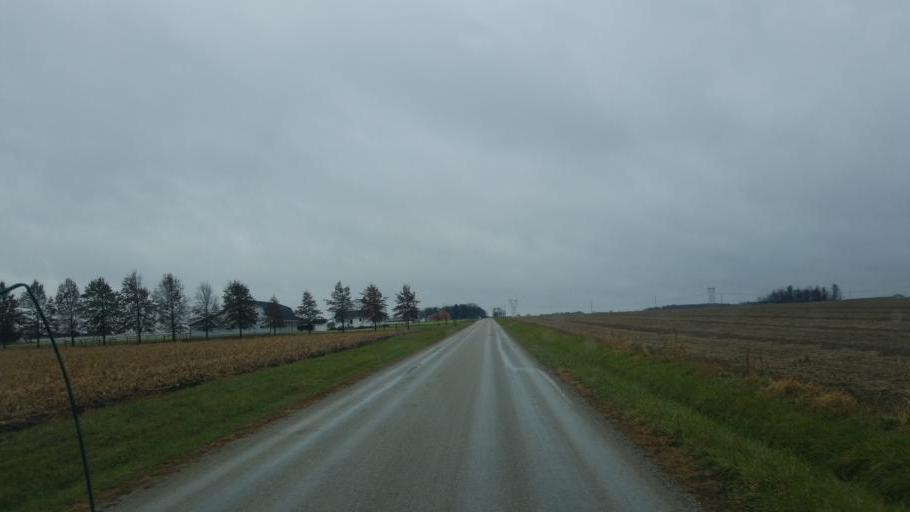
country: US
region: Indiana
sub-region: Adams County
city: Berne
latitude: 40.6923
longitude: -84.9173
